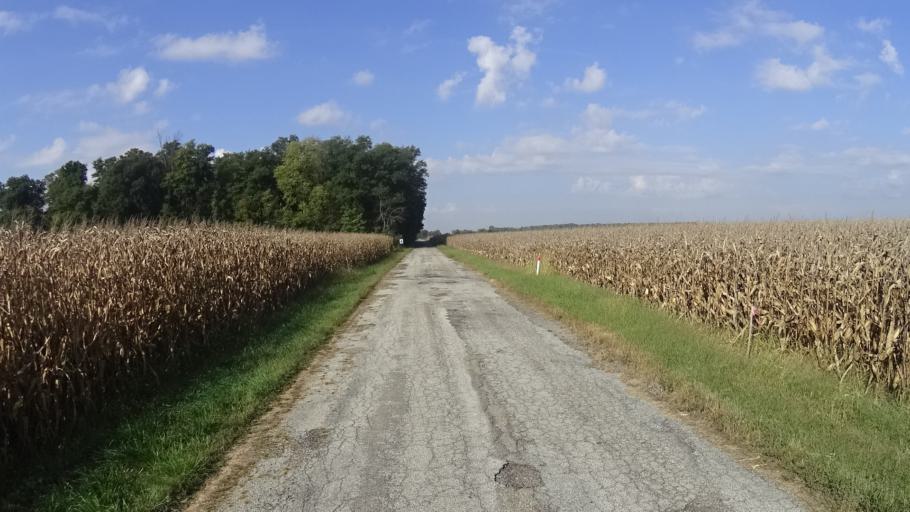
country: US
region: Indiana
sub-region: Madison County
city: Lapel
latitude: 40.0315
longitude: -85.8245
